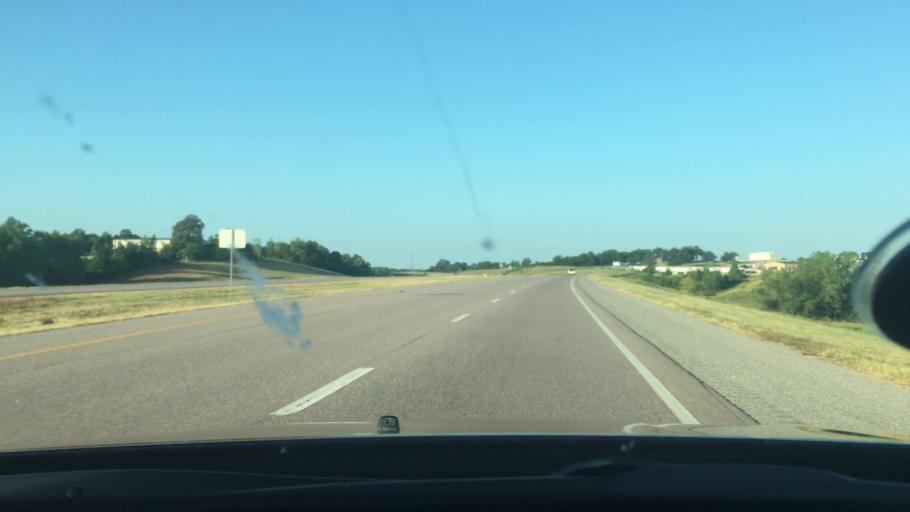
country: US
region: Oklahoma
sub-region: Pontotoc County
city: Byng
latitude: 34.8342
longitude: -96.6906
